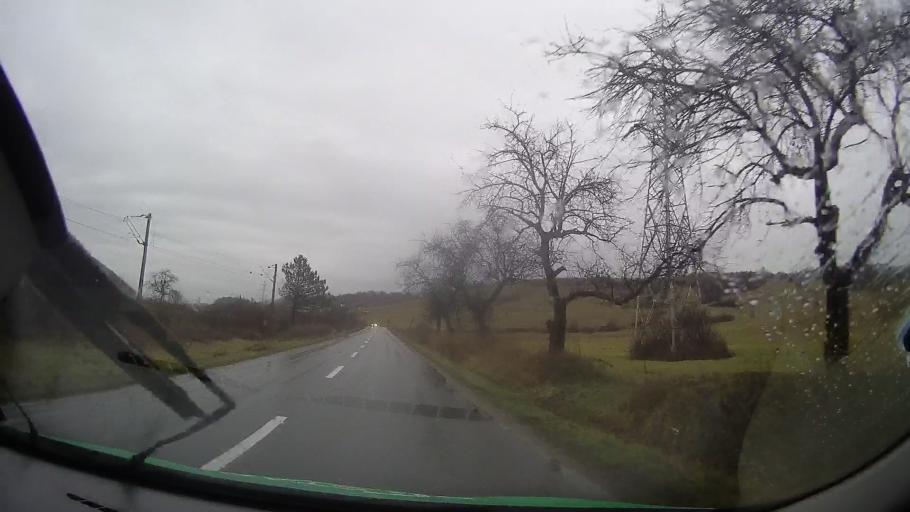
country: RO
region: Bistrita-Nasaud
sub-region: Municipiul Bistrita
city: Viisoara
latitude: 47.0462
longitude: 24.4643
